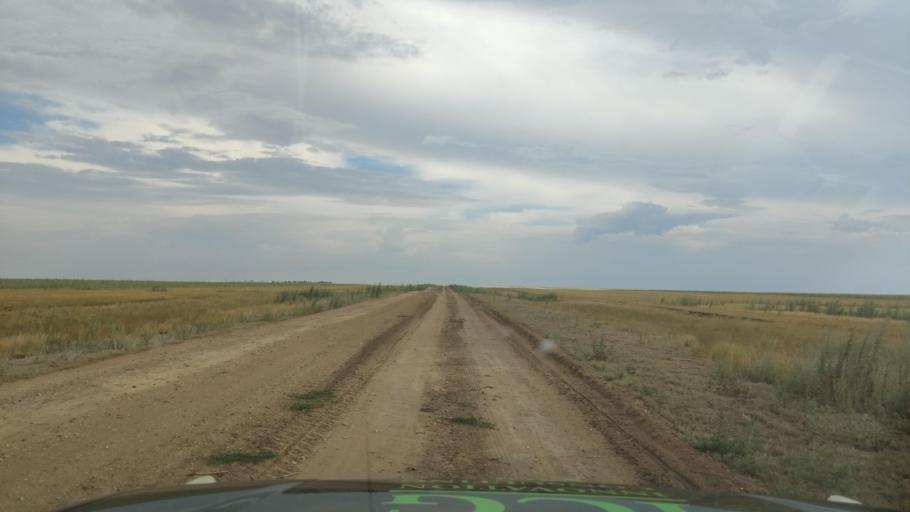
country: KZ
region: Pavlodar
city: Pavlodar
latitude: 52.5346
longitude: 77.5713
